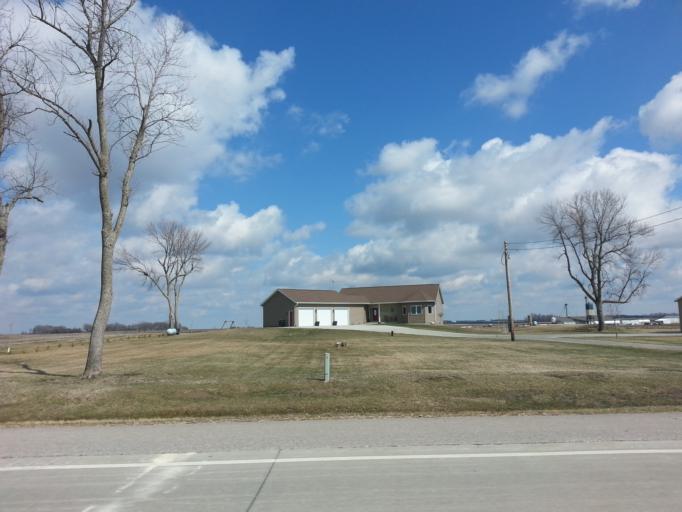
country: US
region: Minnesota
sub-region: Dodge County
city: Dodge Center
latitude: 44.1200
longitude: -92.8995
